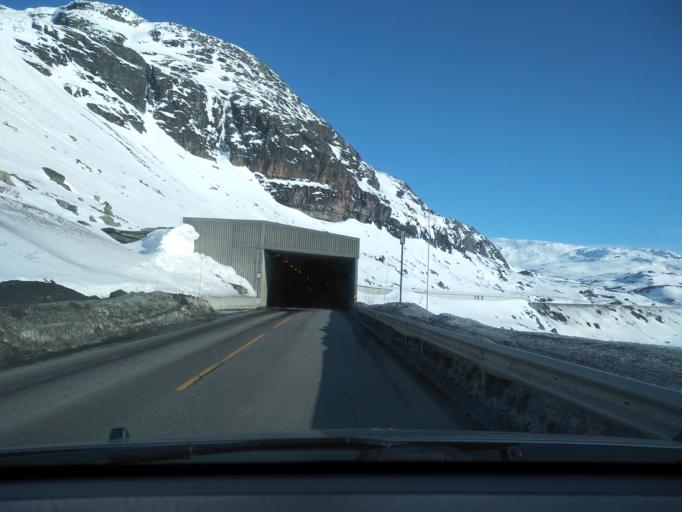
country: NO
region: Hordaland
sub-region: Odda
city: Odda
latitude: 59.8489
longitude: 6.9585
